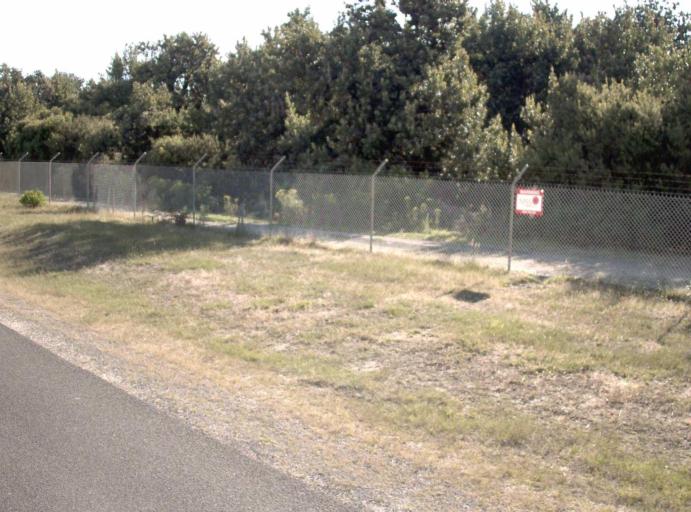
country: AU
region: Victoria
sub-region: Latrobe
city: Morwell
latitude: -38.7127
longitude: 146.3963
